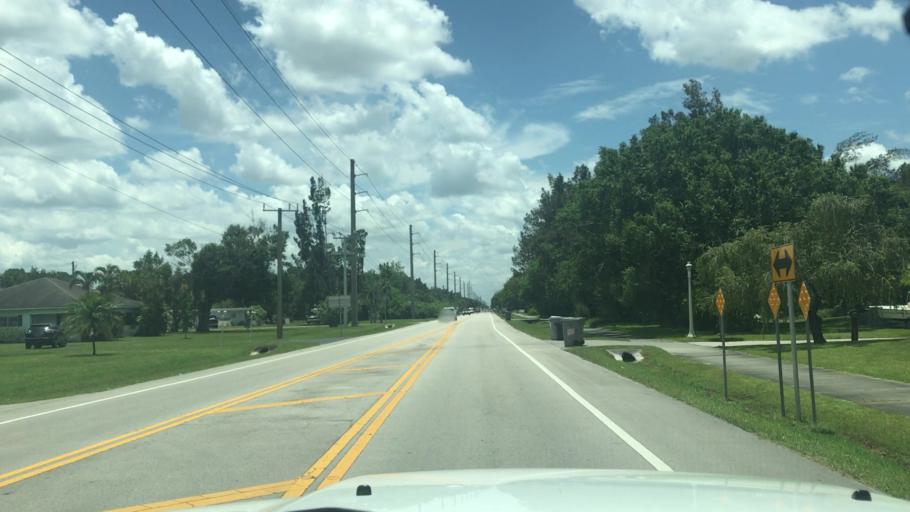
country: US
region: Florida
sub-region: Indian River County
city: Vero Beach South
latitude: 27.6228
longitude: -80.4139
